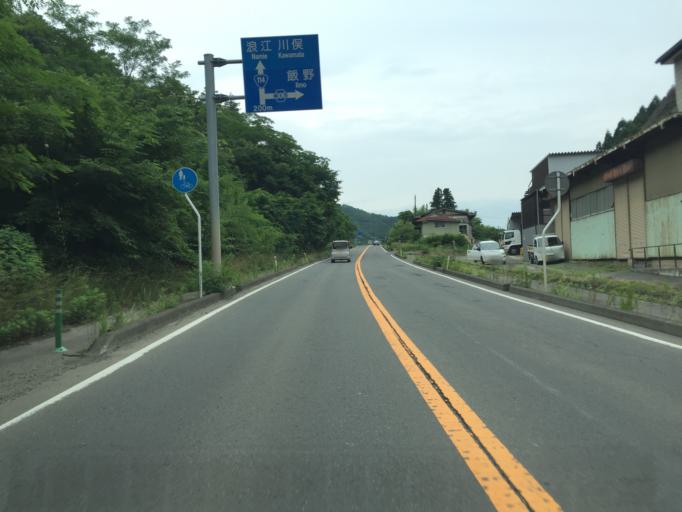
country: JP
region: Fukushima
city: Fukushima-shi
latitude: 37.7048
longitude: 140.5079
